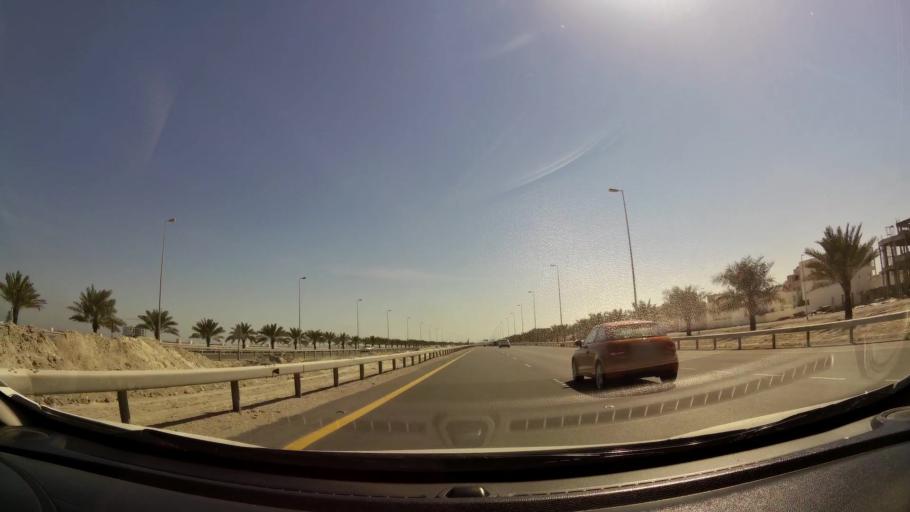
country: BH
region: Muharraq
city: Al Hadd
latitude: 26.2665
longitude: 50.6617
